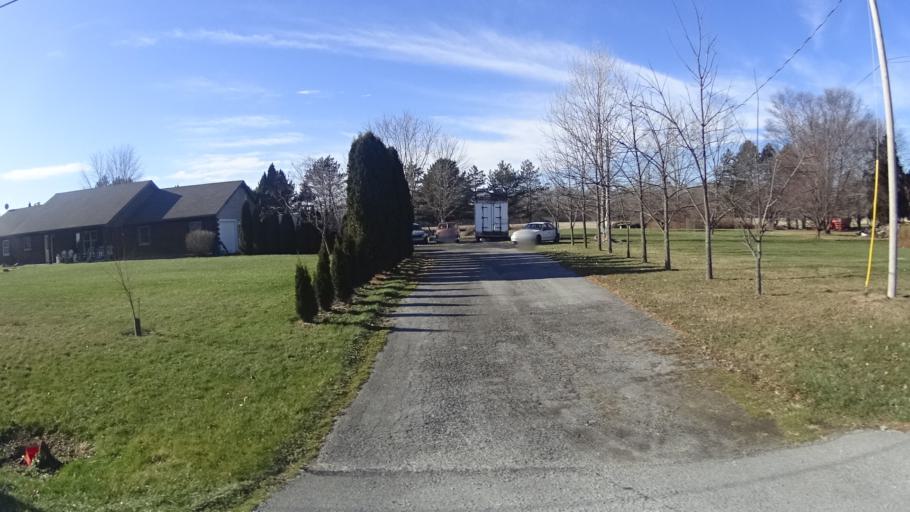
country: US
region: Ohio
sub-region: Huron County
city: Wakeman
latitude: 41.3110
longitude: -82.3434
